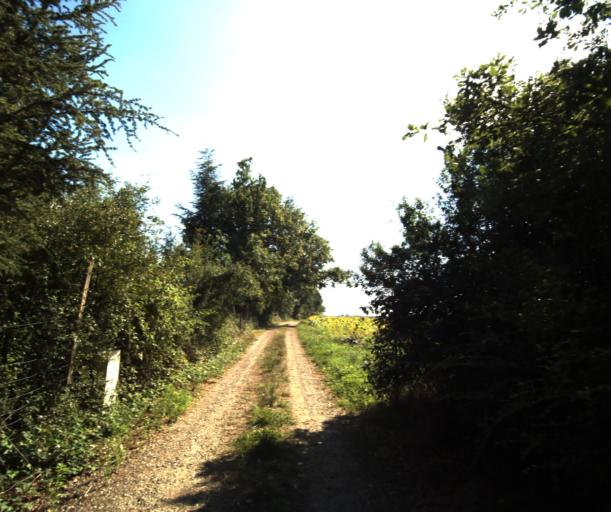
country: FR
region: Midi-Pyrenees
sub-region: Departement de la Haute-Garonne
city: Fonsorbes
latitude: 43.5044
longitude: 1.2170
